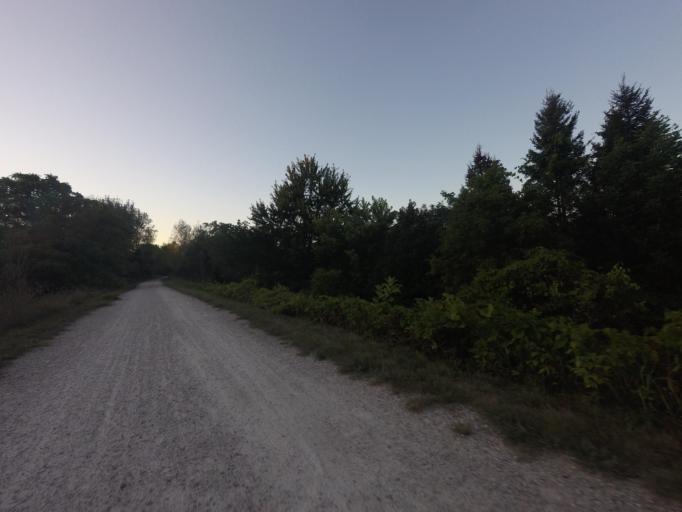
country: CA
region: Ontario
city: Brampton
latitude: 43.9123
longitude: -79.8392
